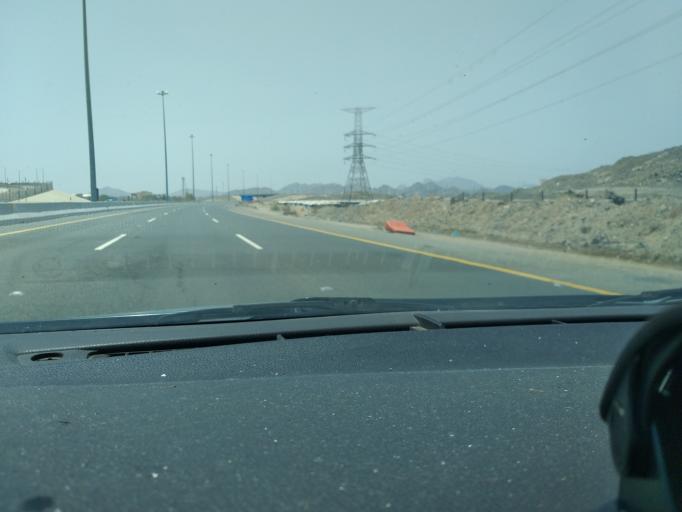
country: SA
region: Makkah
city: Mecca
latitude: 21.3264
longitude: 39.9742
